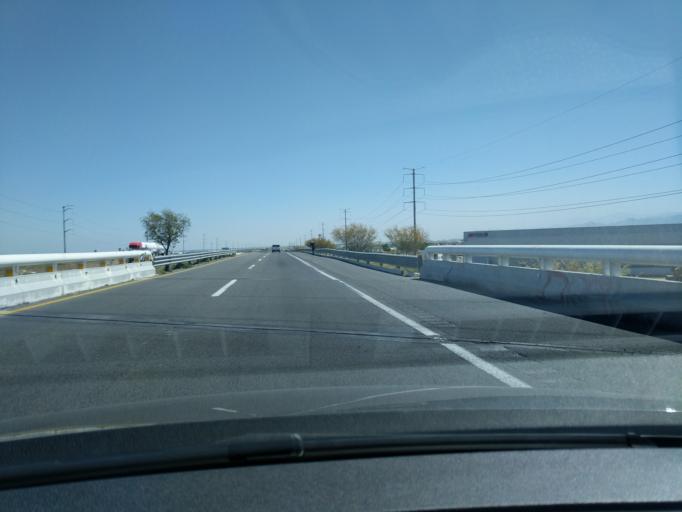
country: MX
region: Nuevo Leon
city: Apodaca
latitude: 25.7691
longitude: -100.1546
